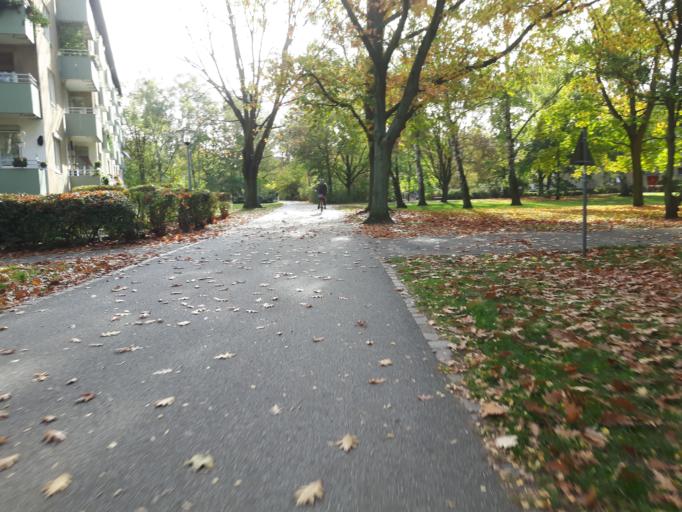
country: DE
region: Berlin
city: Spandau
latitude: 52.5396
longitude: 13.1937
